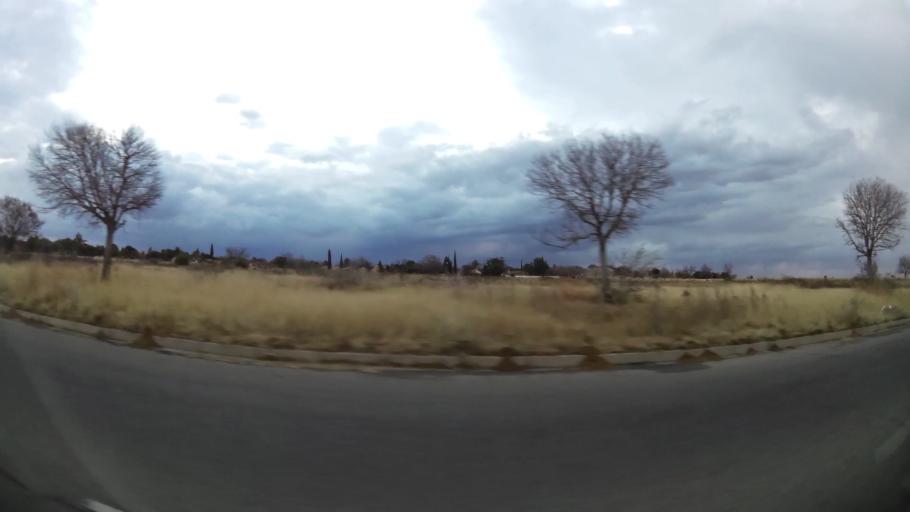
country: ZA
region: Orange Free State
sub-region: Lejweleputswa District Municipality
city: Welkom
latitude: -27.9591
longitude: 26.7530
